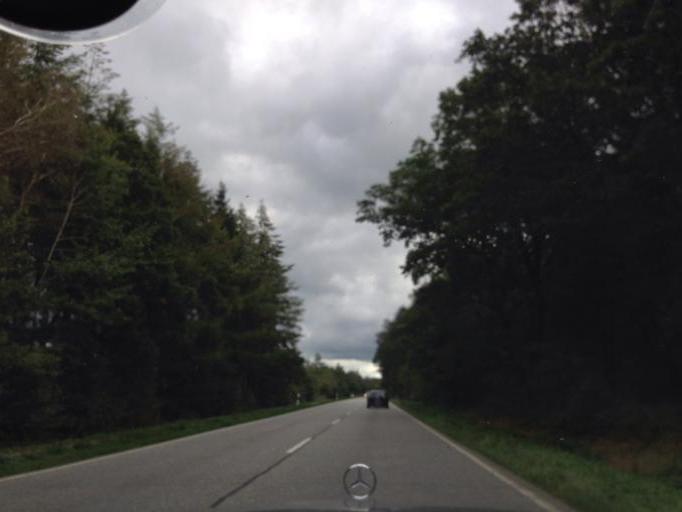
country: DE
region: Schleswig-Holstein
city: Leck
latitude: 54.7532
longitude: 9.0032
